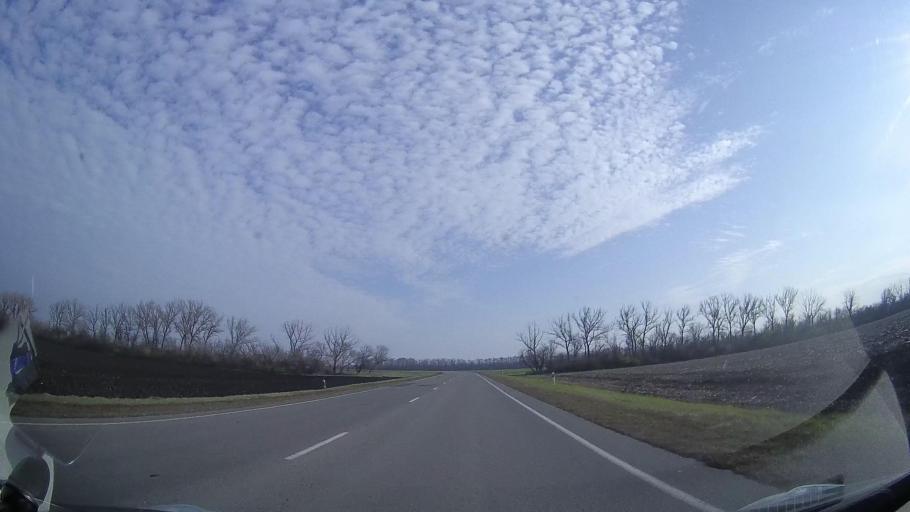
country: RU
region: Rostov
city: Tselina
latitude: 46.5214
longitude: 41.1489
